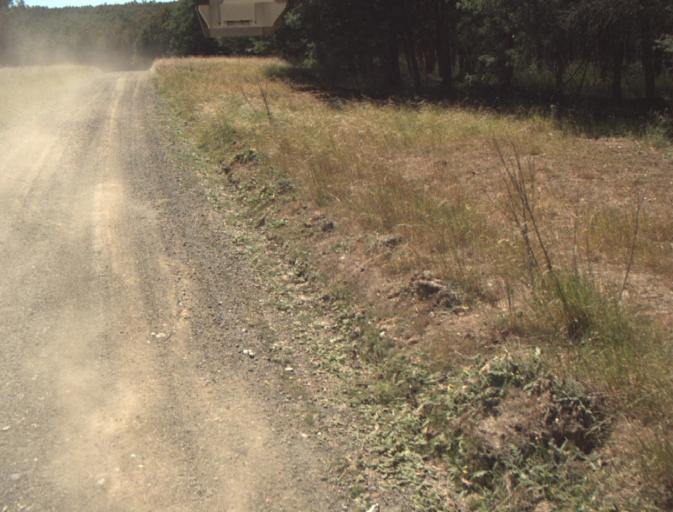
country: AU
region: Tasmania
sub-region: Dorset
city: Scottsdale
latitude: -41.2722
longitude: 147.3488
